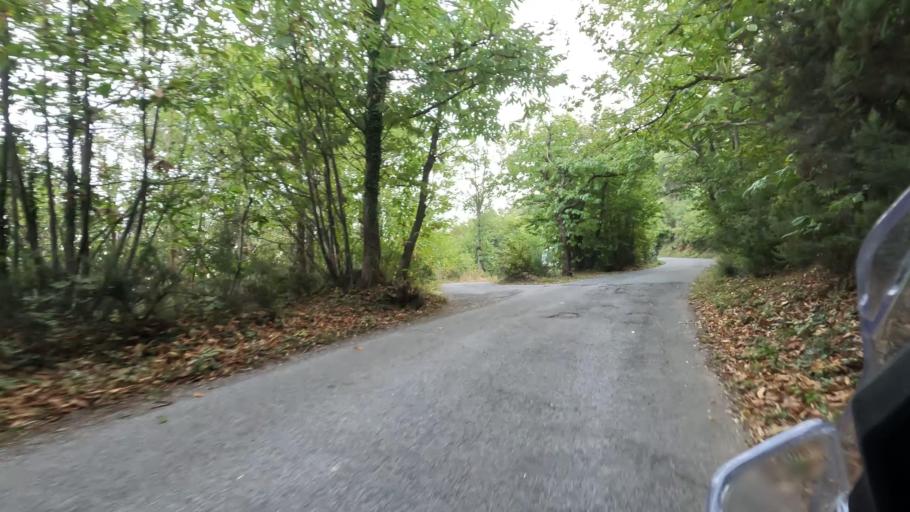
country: IT
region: Liguria
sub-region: Provincia di Savona
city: San Giovanni
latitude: 44.3959
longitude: 8.5347
